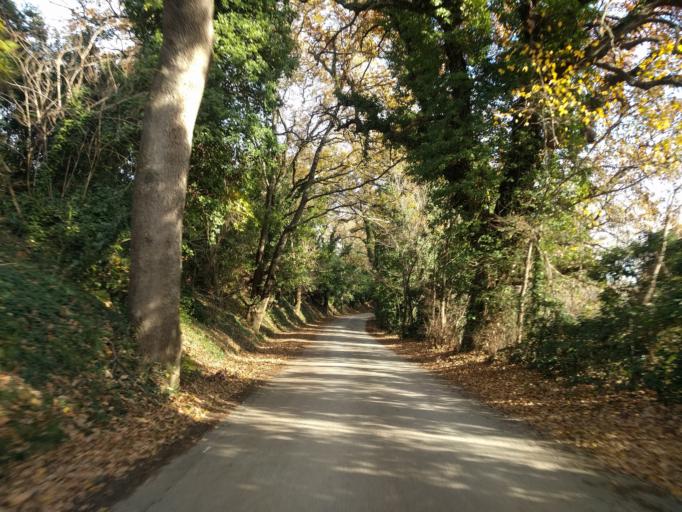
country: IT
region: The Marches
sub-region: Provincia di Pesaro e Urbino
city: Cuccurano
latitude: 43.8110
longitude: 12.9646
